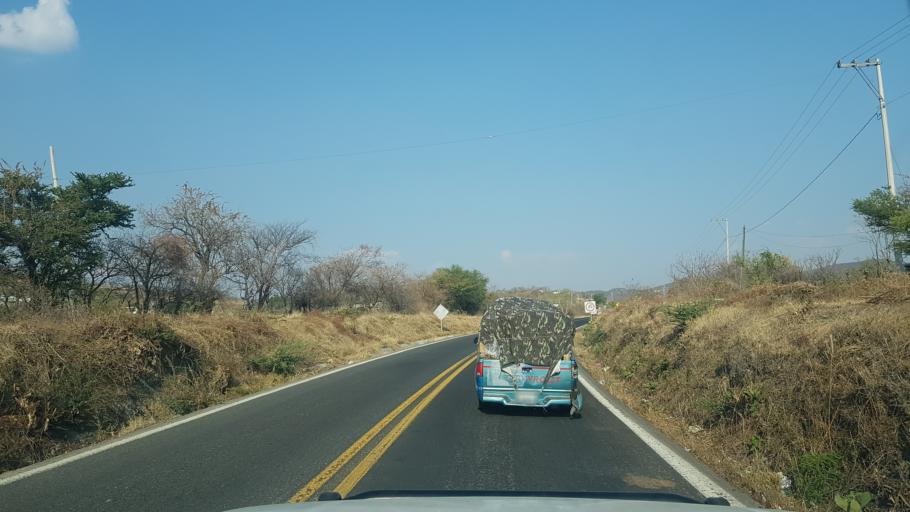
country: MX
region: Puebla
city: Calmeca
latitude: 18.6437
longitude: -98.6334
